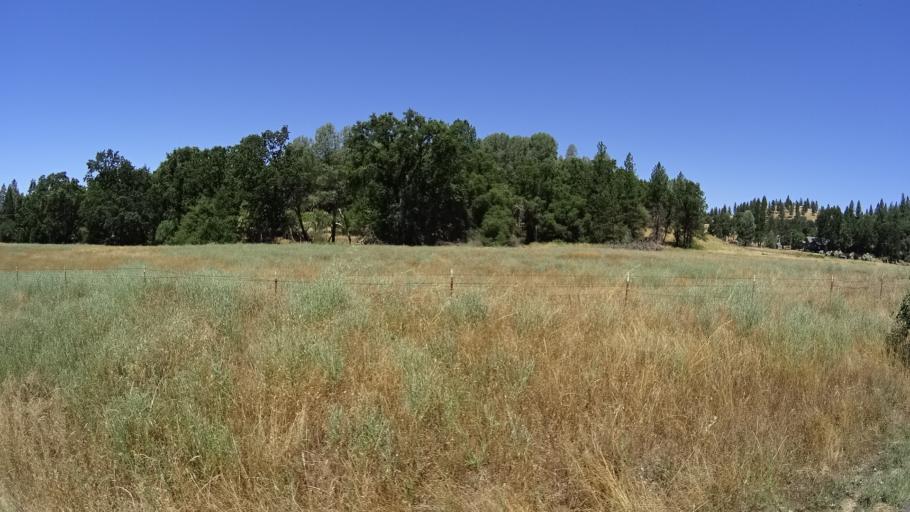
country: US
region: California
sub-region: Calaveras County
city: Mountain Ranch
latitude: 38.2068
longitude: -120.5526
